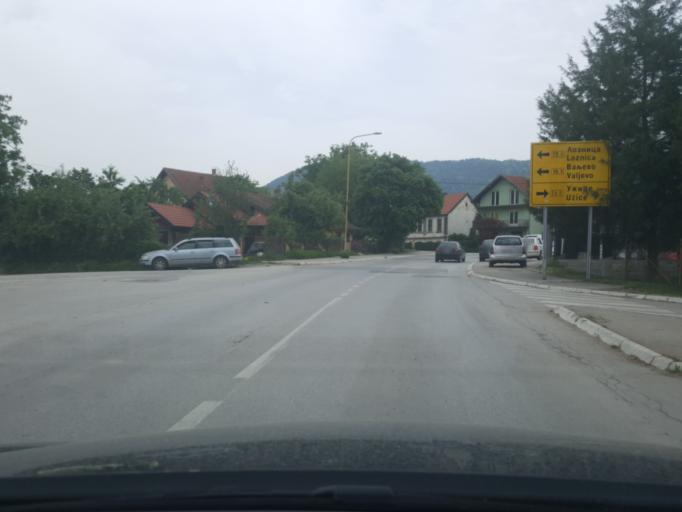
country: RS
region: Central Serbia
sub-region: Zlatiborski Okrug
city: Bajina Basta
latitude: 43.9736
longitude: 19.5684
